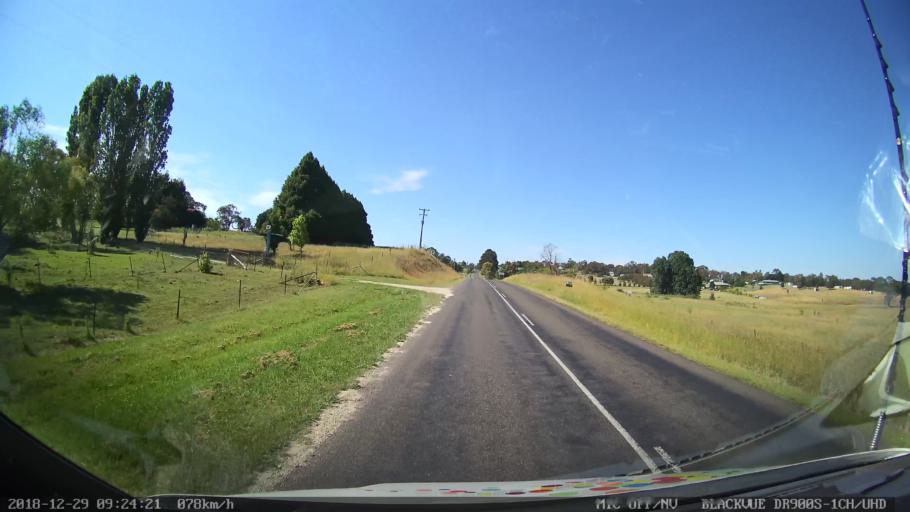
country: AU
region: New South Wales
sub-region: Upper Lachlan Shire
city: Crookwell
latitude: -34.5353
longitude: 149.3944
